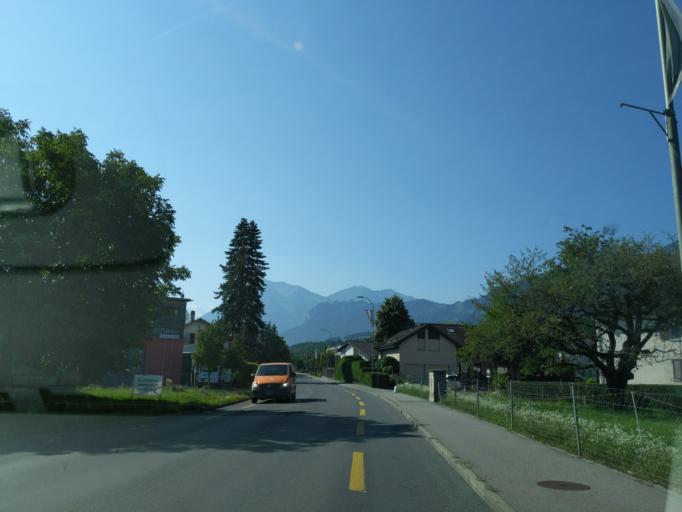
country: CH
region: Bern
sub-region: Thun District
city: Thun
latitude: 46.7415
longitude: 7.5986
